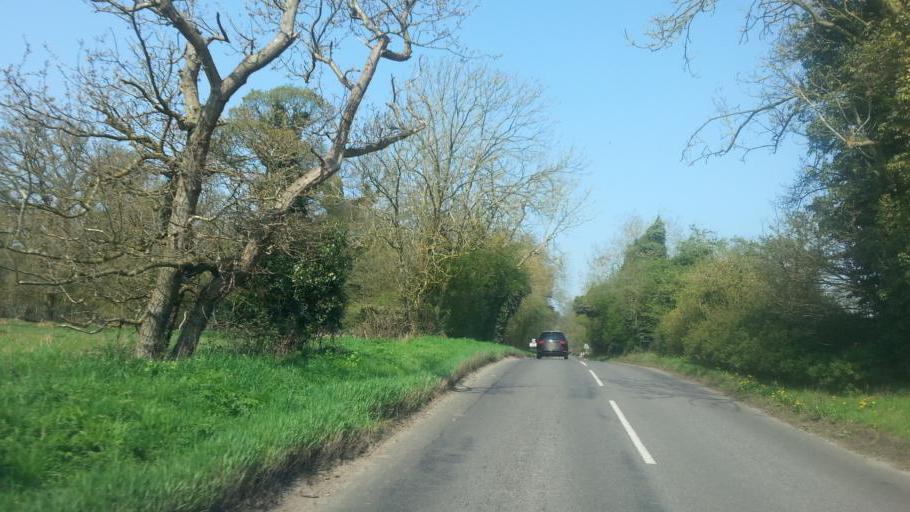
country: GB
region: England
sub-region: Suffolk
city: Thurston
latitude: 52.2431
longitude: 0.8205
